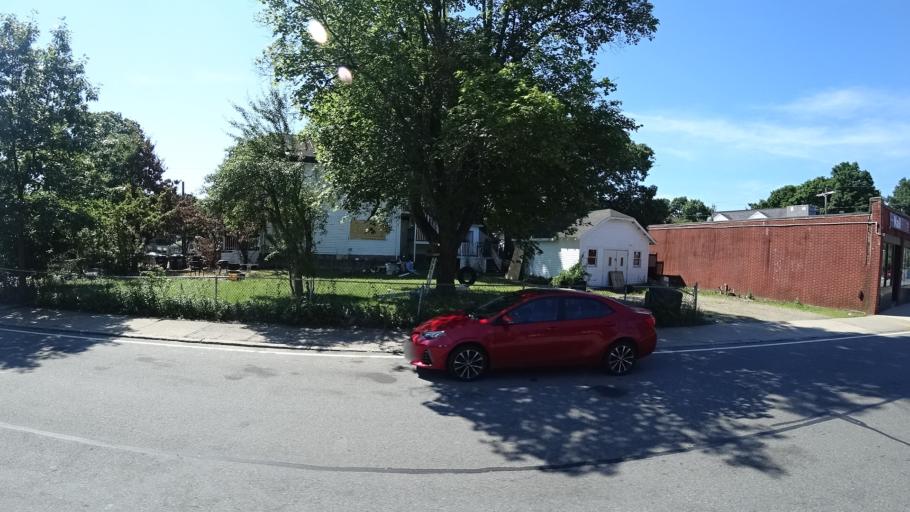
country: US
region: Massachusetts
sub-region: Norfolk County
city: Dedham
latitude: 42.2411
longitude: -71.1542
